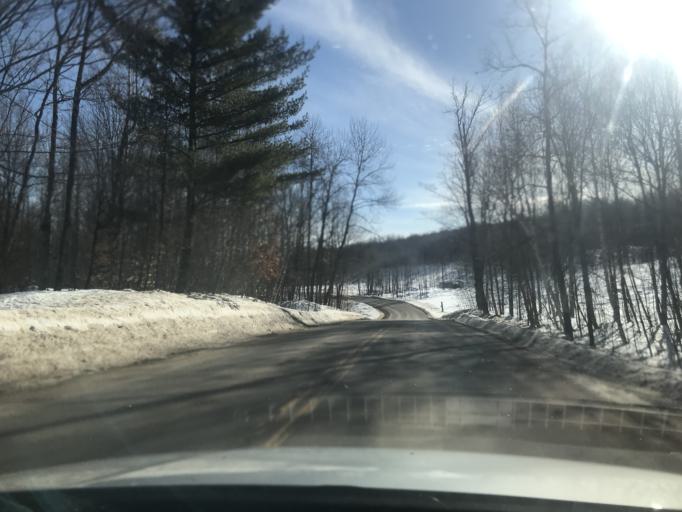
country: US
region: Michigan
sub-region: Dickinson County
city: Kingsford
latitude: 45.4052
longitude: -88.3799
